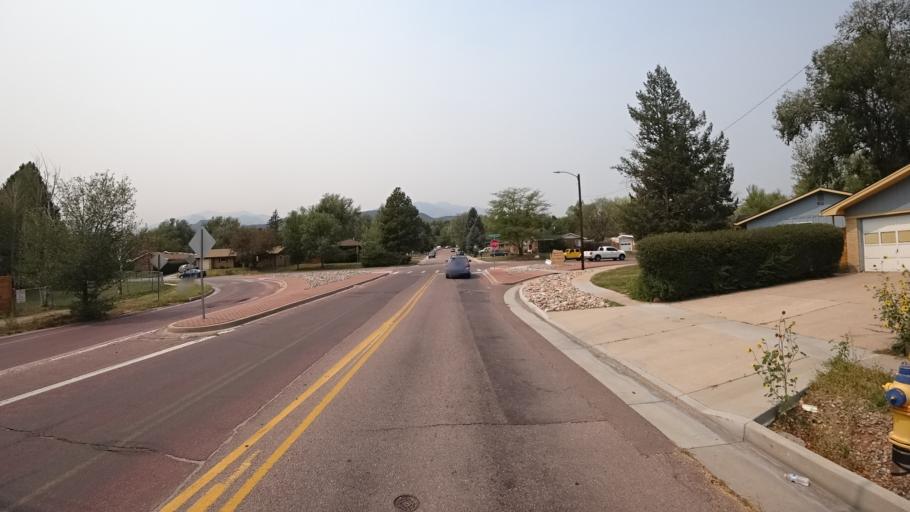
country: US
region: Colorado
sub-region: El Paso County
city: Colorado Springs
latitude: 38.8089
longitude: -104.8455
